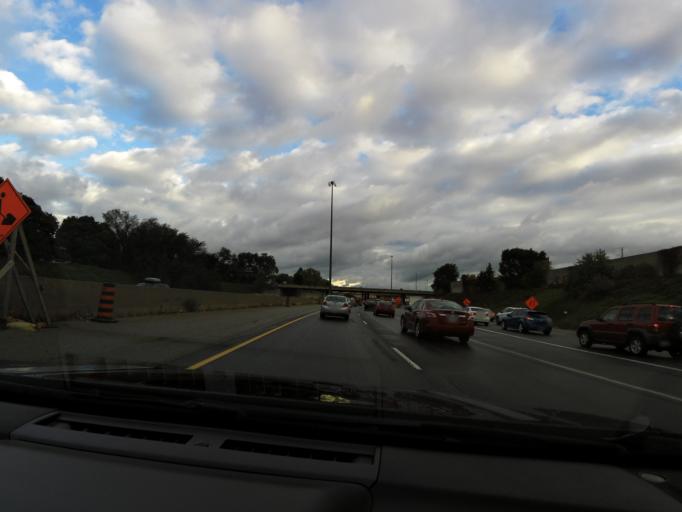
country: CA
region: Ontario
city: Waterloo
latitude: 43.4575
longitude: -80.4710
